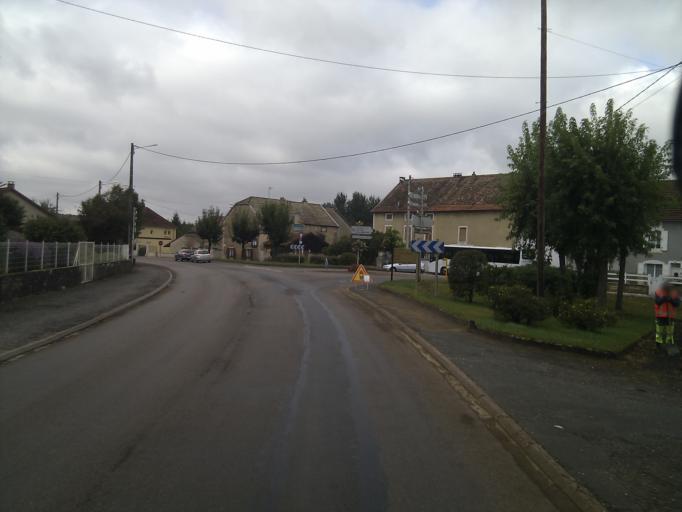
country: FR
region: Champagne-Ardenne
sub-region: Departement de la Haute-Marne
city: Doulaincourt-Saucourt
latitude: 48.2553
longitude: 5.3339
